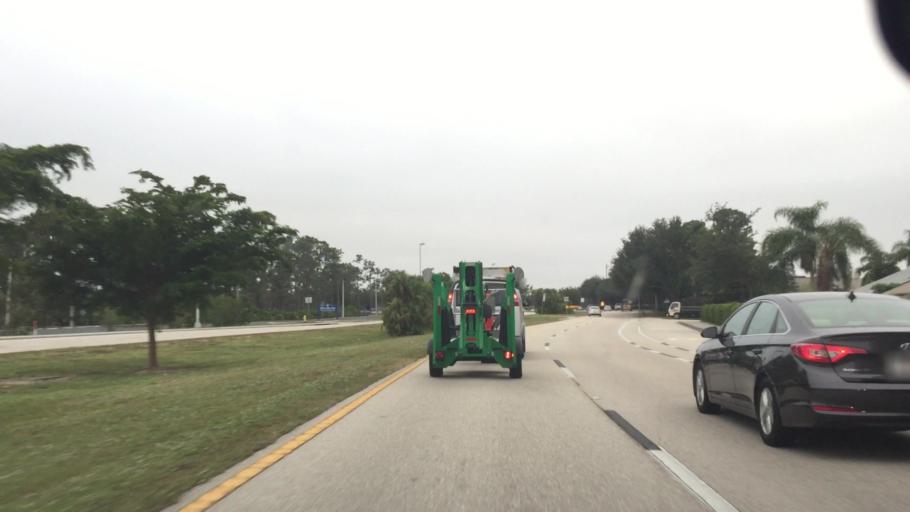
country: US
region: Florida
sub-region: Lee County
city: Three Oaks
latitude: 26.4772
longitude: -81.7946
